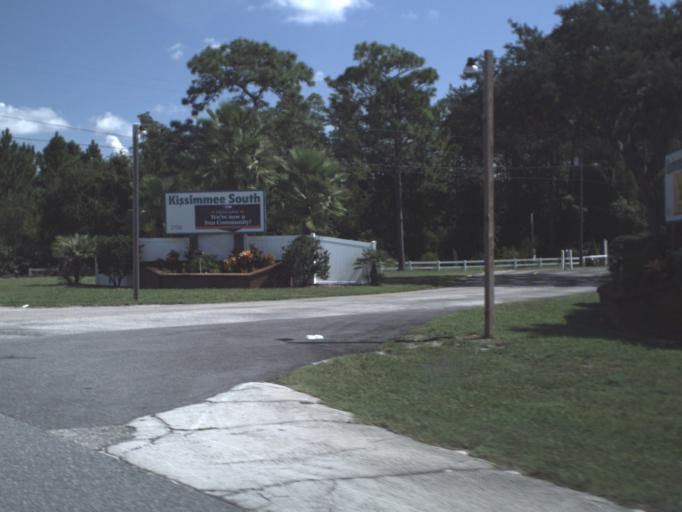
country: US
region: Florida
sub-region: Polk County
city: Loughman
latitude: 28.2088
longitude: -81.5763
